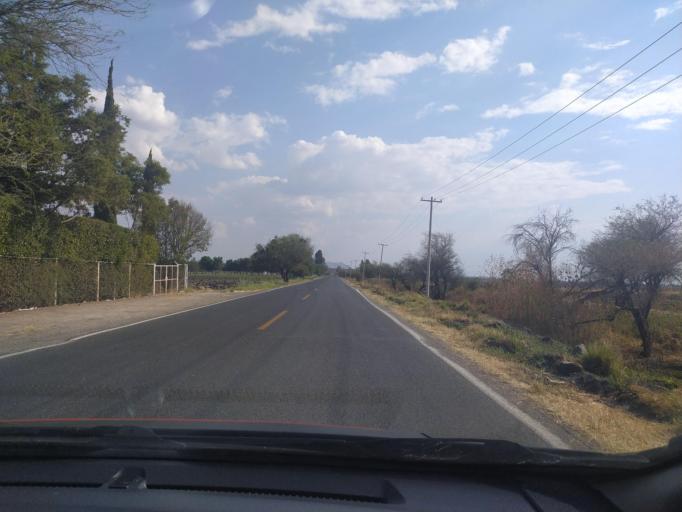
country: MX
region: Guanajuato
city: San Roque
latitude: 20.9418
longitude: -101.8557
